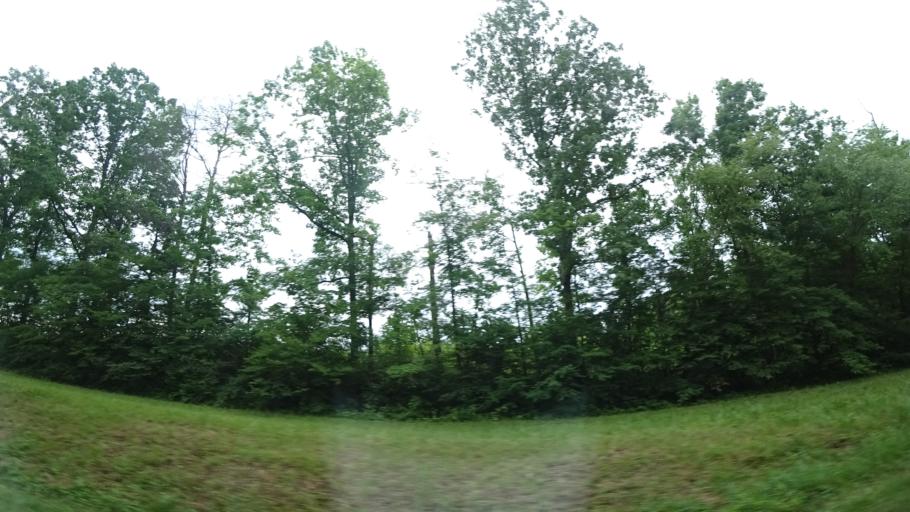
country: US
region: Virginia
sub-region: Spotsylvania County
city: Spotsylvania Courthouse
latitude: 38.1187
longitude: -77.7448
